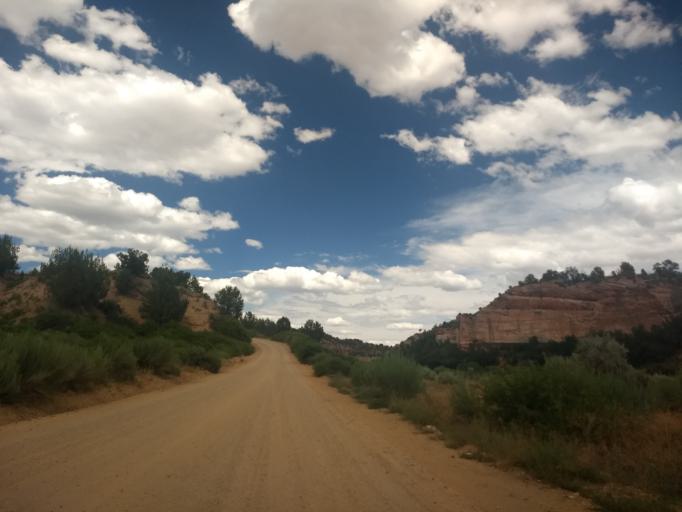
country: US
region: Utah
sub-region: Kane County
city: Kanab
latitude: 37.1456
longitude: -112.5406
